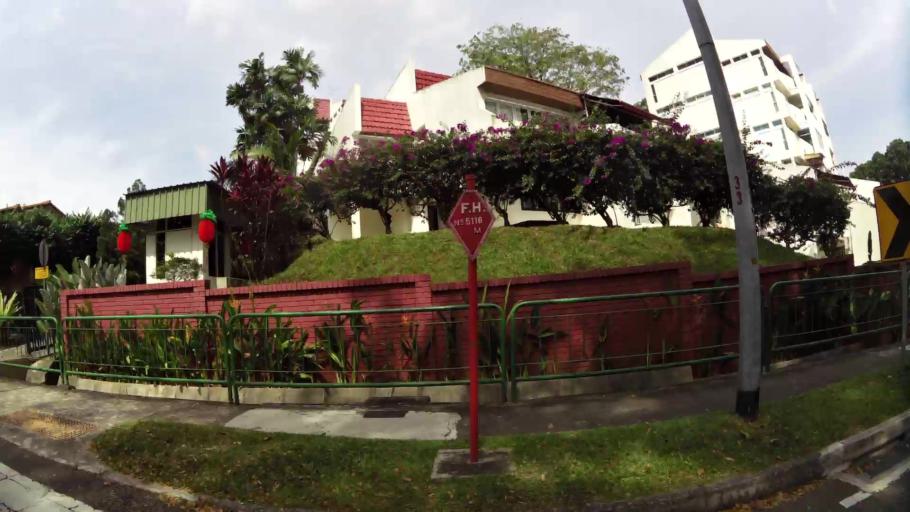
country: SG
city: Singapore
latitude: 1.3277
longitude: 103.7664
